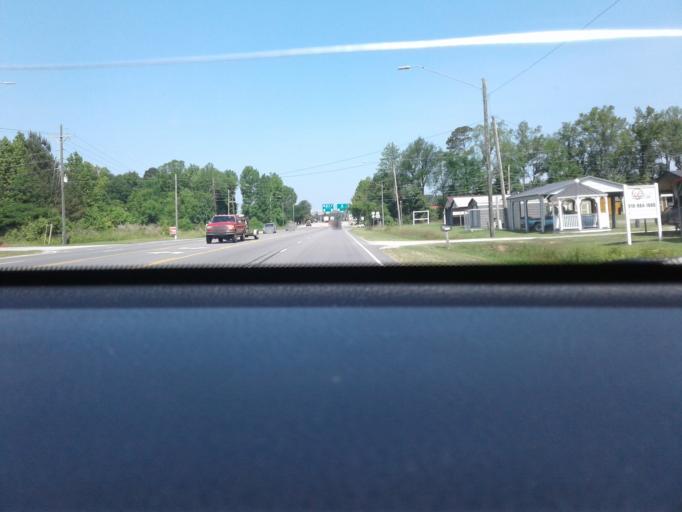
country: US
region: North Carolina
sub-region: Harnett County
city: Lillington
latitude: 35.4159
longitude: -78.7989
